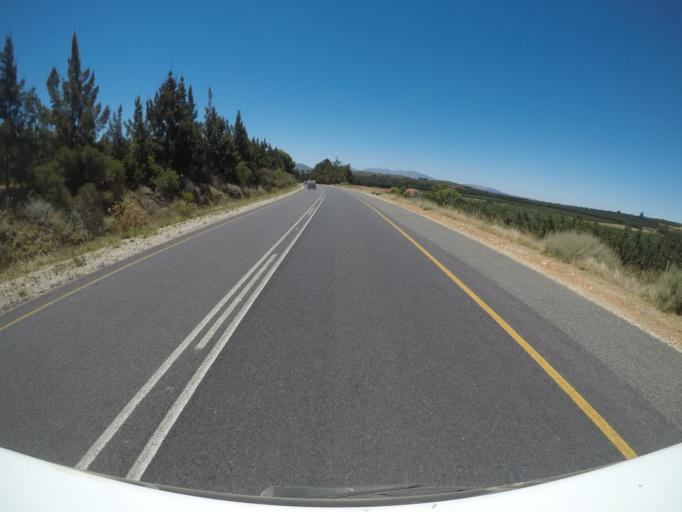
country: ZA
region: Western Cape
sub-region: Overberg District Municipality
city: Grabouw
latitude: -34.0573
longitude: 19.1437
